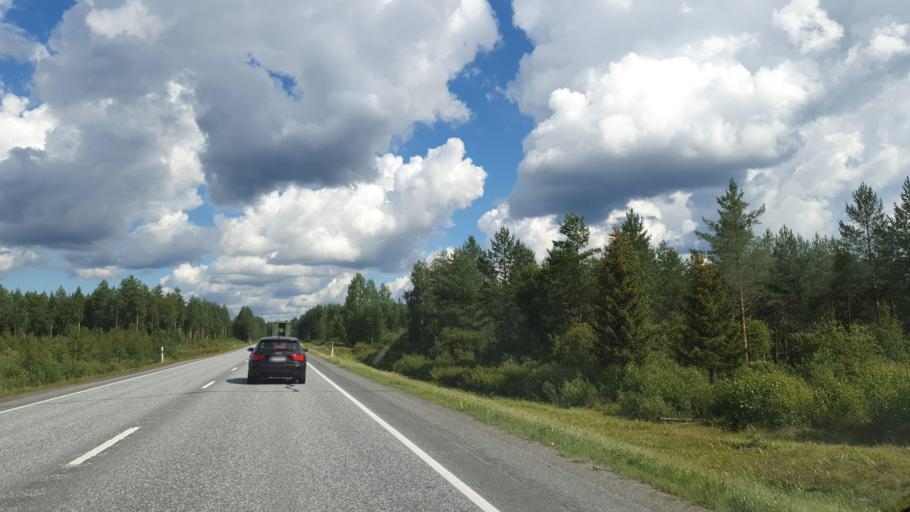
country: FI
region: Kainuu
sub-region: Kajaani
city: Kajaani
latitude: 64.1317
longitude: 27.4818
